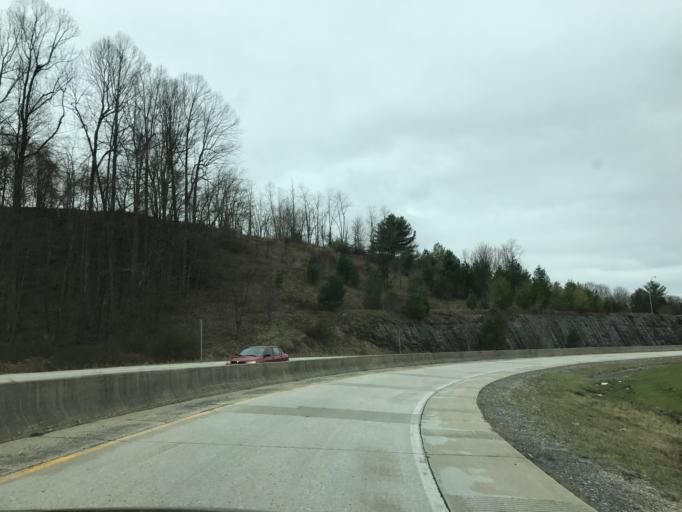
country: US
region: West Virginia
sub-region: Raleigh County
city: Beaver
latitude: 37.7615
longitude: -81.1446
